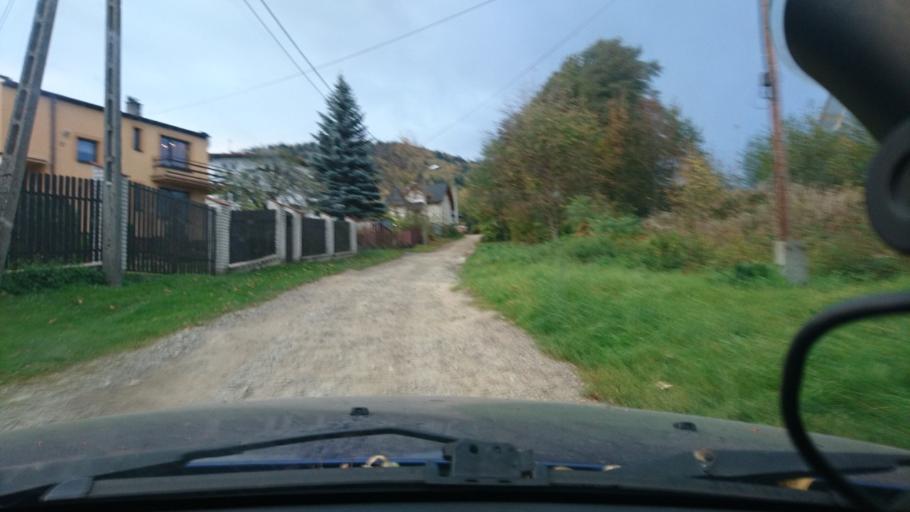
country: PL
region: Silesian Voivodeship
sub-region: Powiat bielski
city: Wilkowice
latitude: 49.7958
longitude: 19.0918
